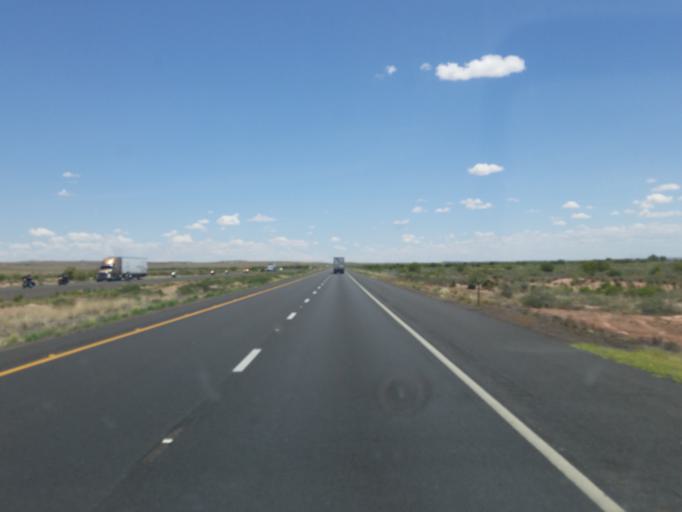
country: US
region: Arizona
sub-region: Navajo County
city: Winslow
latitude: 34.9921
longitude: -110.5756
